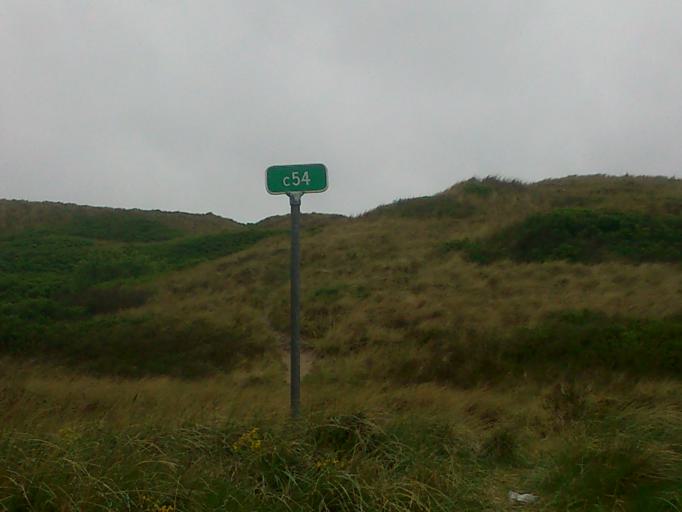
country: DK
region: Central Jutland
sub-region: Ringkobing-Skjern Kommune
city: Hvide Sande
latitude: 56.0066
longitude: 8.1183
